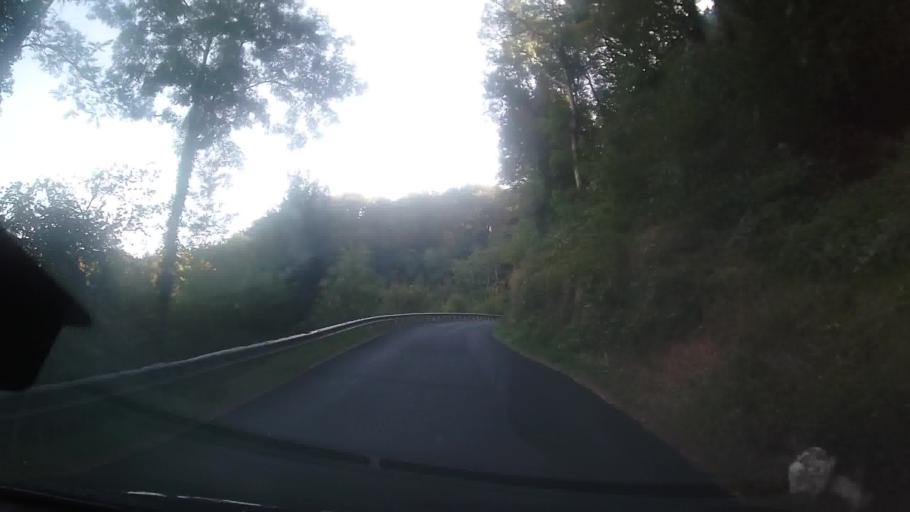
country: FR
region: Aquitaine
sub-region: Departement de la Dordogne
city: Cenac-et-Saint-Julien
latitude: 44.7973
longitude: 1.1896
